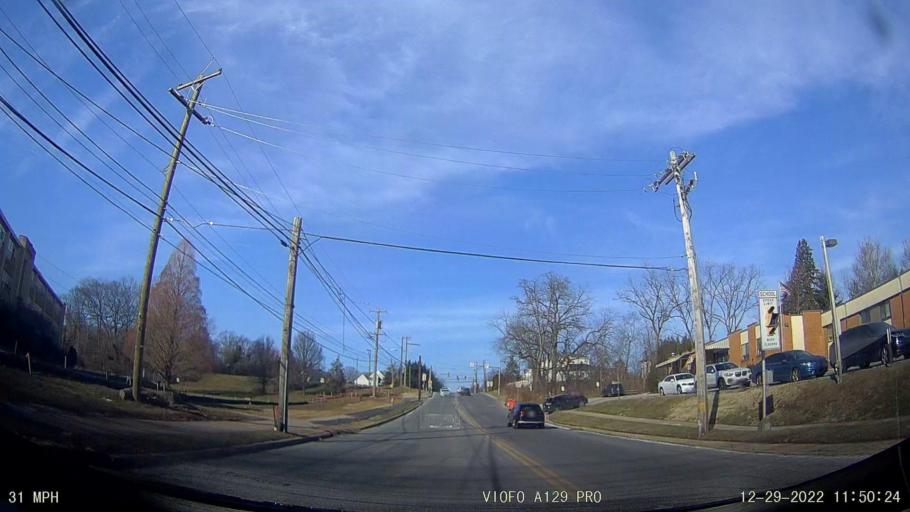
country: US
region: Pennsylvania
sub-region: Montgomery County
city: Norristown
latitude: 40.1282
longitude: -75.3222
